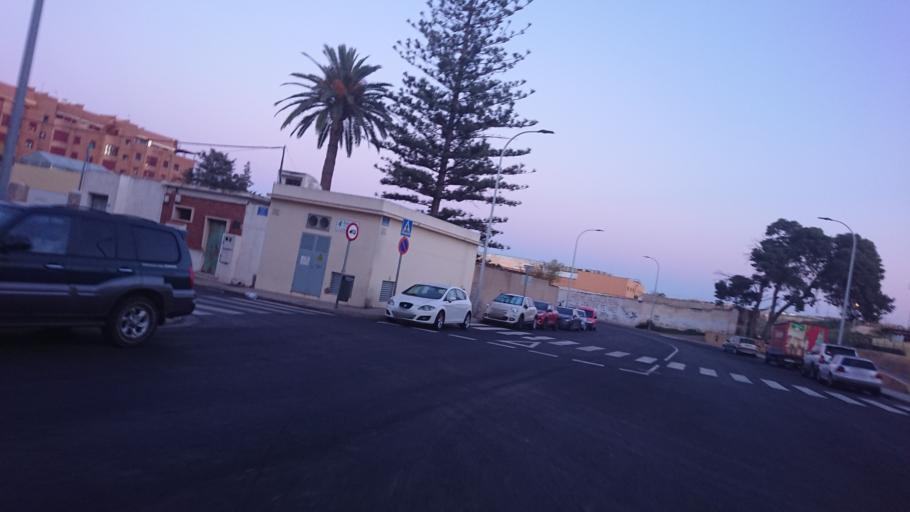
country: ES
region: Melilla
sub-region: Melilla
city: Melilla
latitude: 35.2729
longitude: -2.9468
